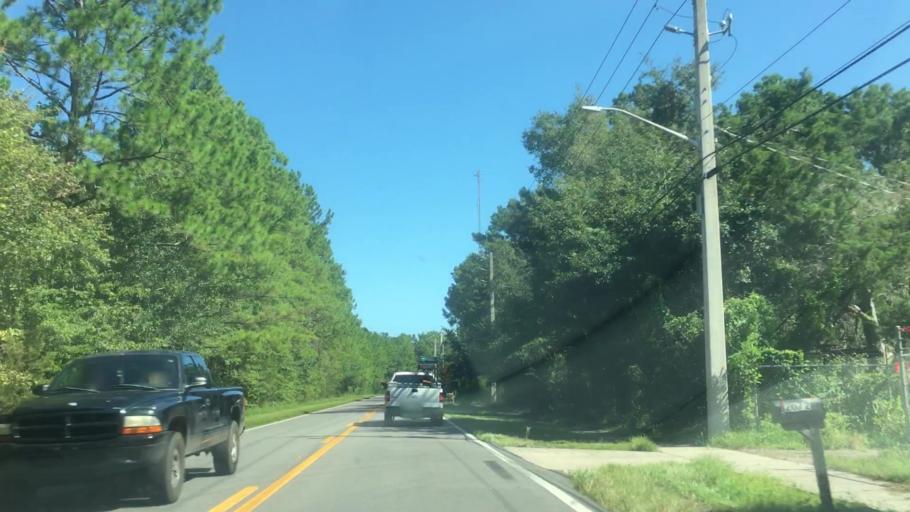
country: US
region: Florida
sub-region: Nassau County
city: Yulee
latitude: 30.4969
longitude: -81.5879
